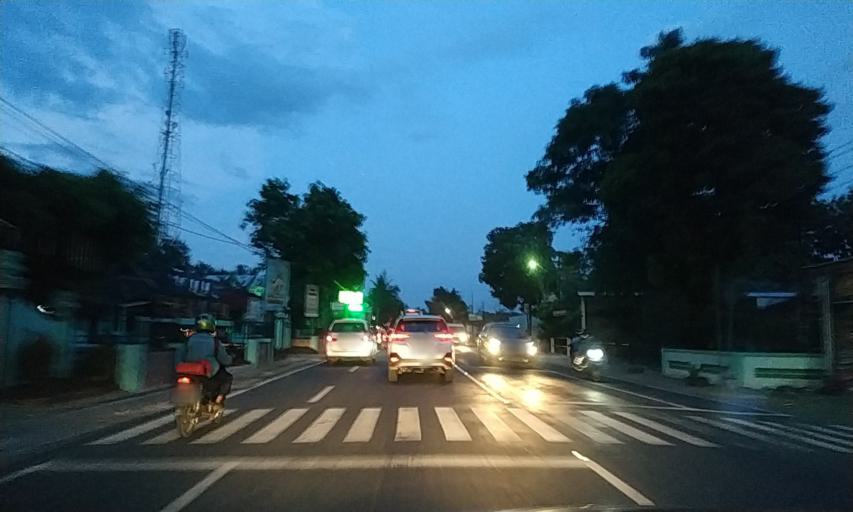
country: ID
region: Daerah Istimewa Yogyakarta
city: Godean
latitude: -7.8141
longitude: 110.2582
